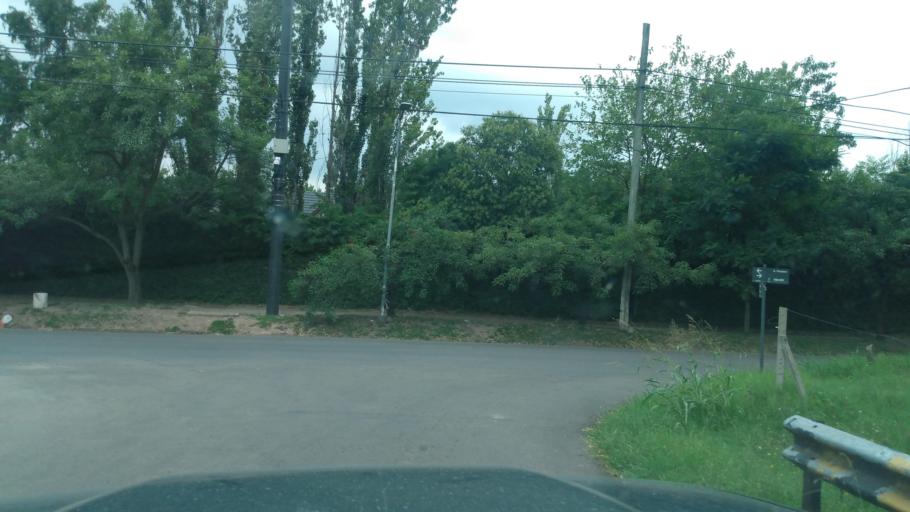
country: AR
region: Buenos Aires
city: Hurlingham
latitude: -34.5765
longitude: -58.7016
